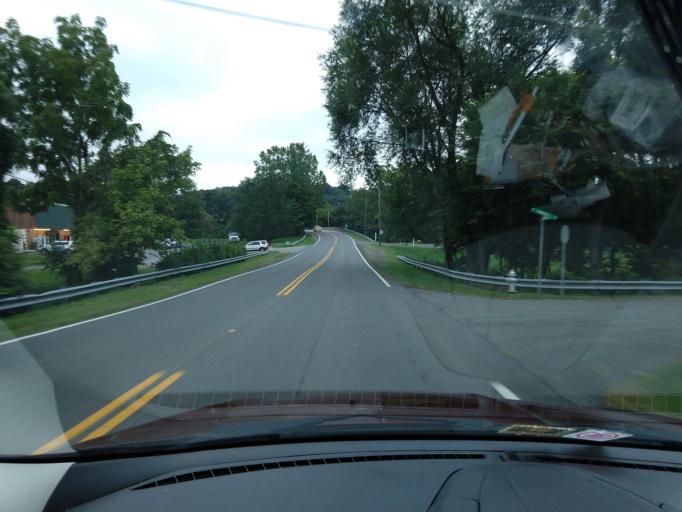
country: US
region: Virginia
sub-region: City of Covington
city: Fairlawn
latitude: 37.7549
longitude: -79.9872
